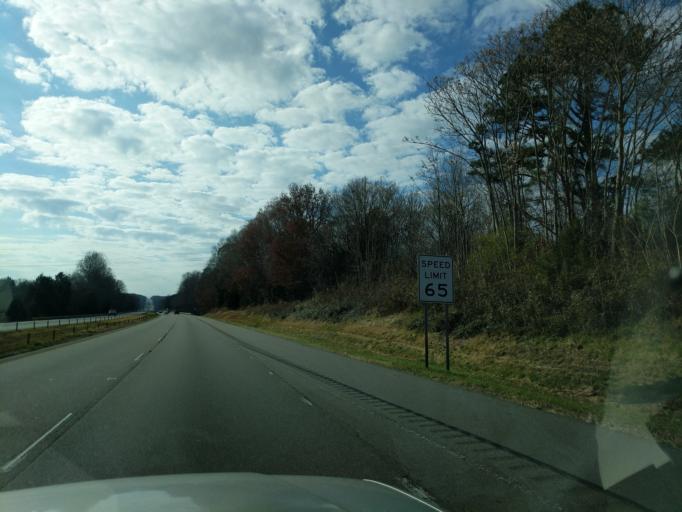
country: US
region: North Carolina
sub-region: Iredell County
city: Statesville
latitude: 35.7931
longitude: -80.9395
